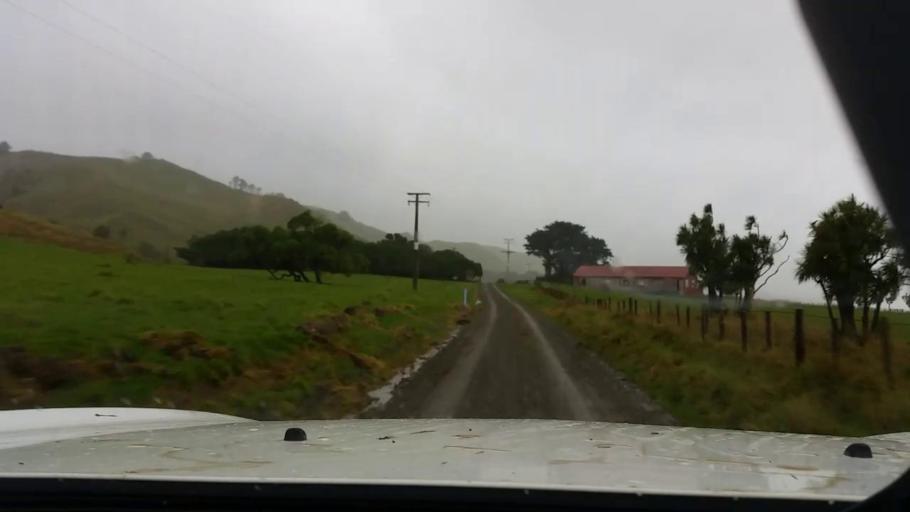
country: NZ
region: Wellington
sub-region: Masterton District
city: Masterton
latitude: -41.2632
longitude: 175.8937
